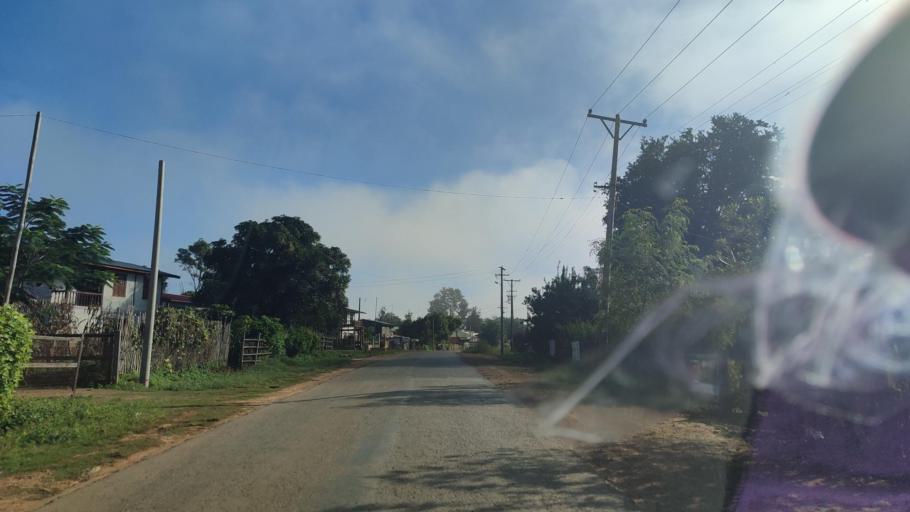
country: MM
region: Shan
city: Taunggyi
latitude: 20.9276
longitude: 97.6586
